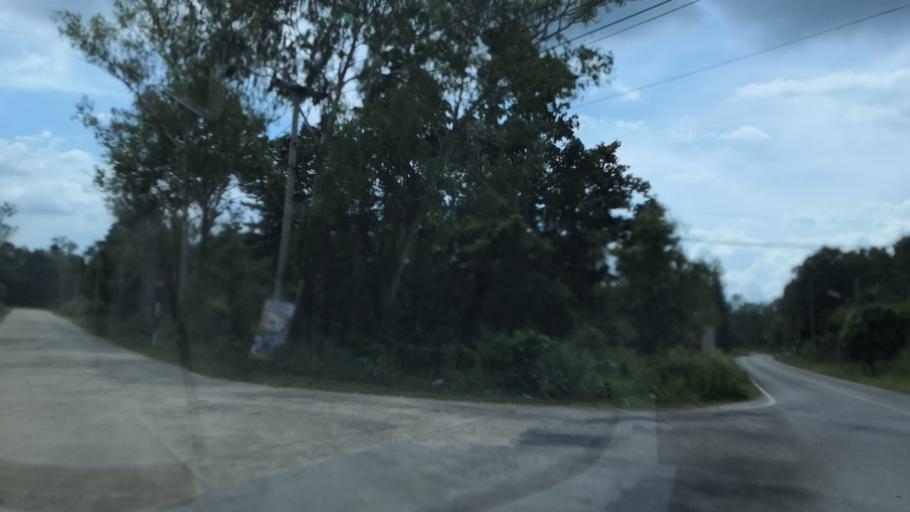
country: TH
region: Mae Hong Son
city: Khun Yuam
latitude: 18.8218
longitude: 97.9272
